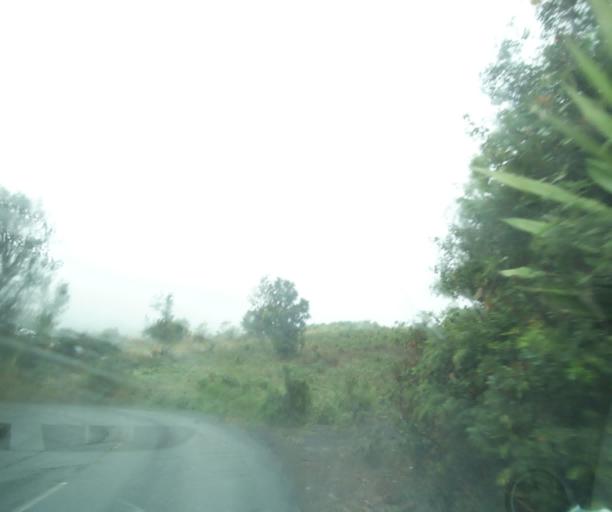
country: RE
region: Reunion
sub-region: Reunion
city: Saint-Paul
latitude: -21.0141
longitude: 55.3089
